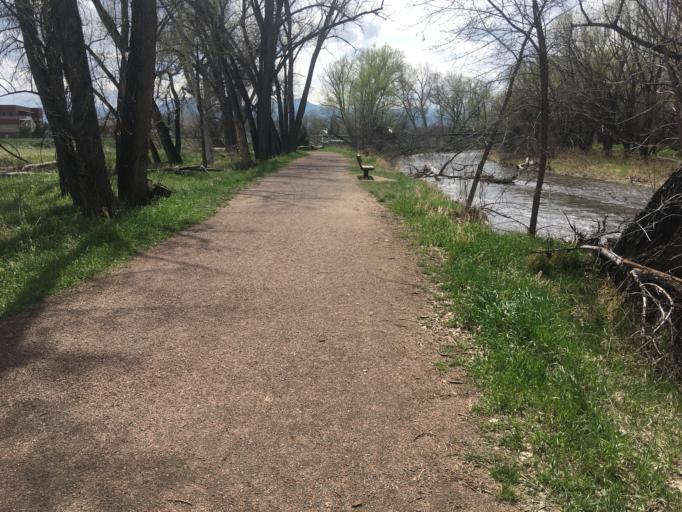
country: US
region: Colorado
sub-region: Boulder County
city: Gunbarrel
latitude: 40.0505
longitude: -105.1816
